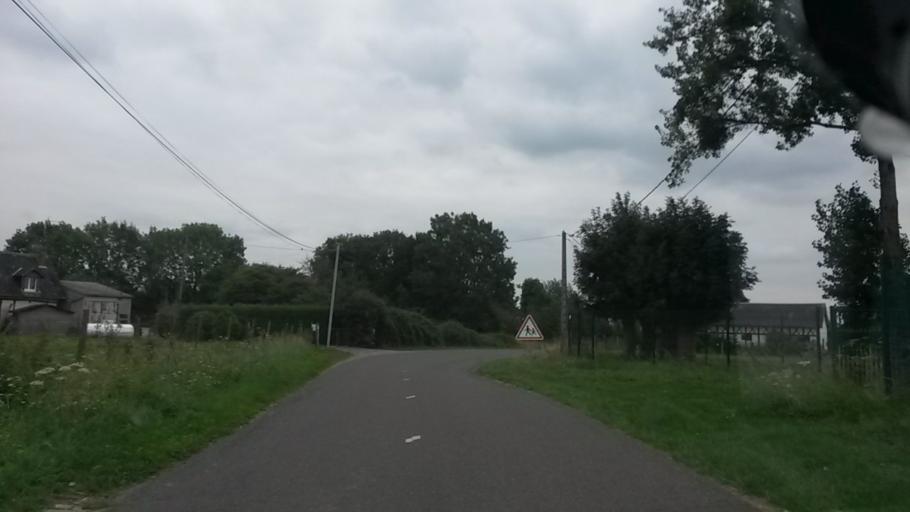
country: FR
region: Haute-Normandie
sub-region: Departement de la Seine-Maritime
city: La Feuillie
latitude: 49.4728
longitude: 1.5289
